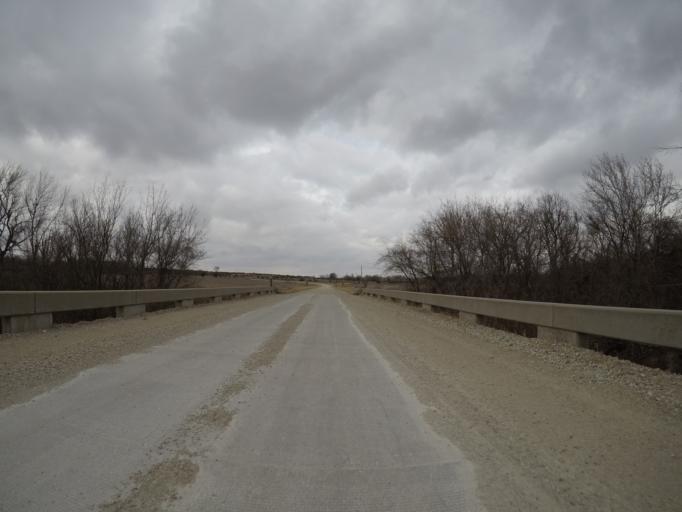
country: US
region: Kansas
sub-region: Morris County
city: Council Grove
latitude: 38.7655
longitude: -96.2810
